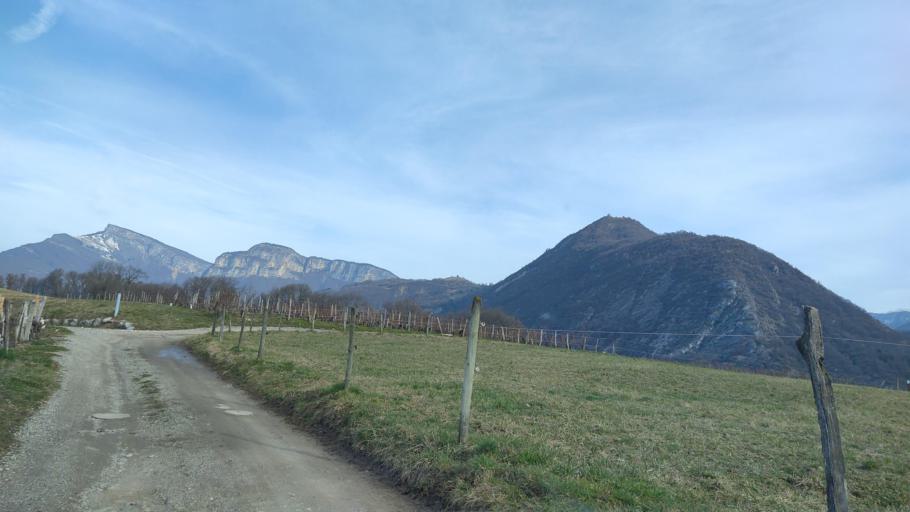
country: FR
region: Rhone-Alpes
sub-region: Departement de la Savoie
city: Challes-les-Eaux
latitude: 45.5346
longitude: 5.9886
